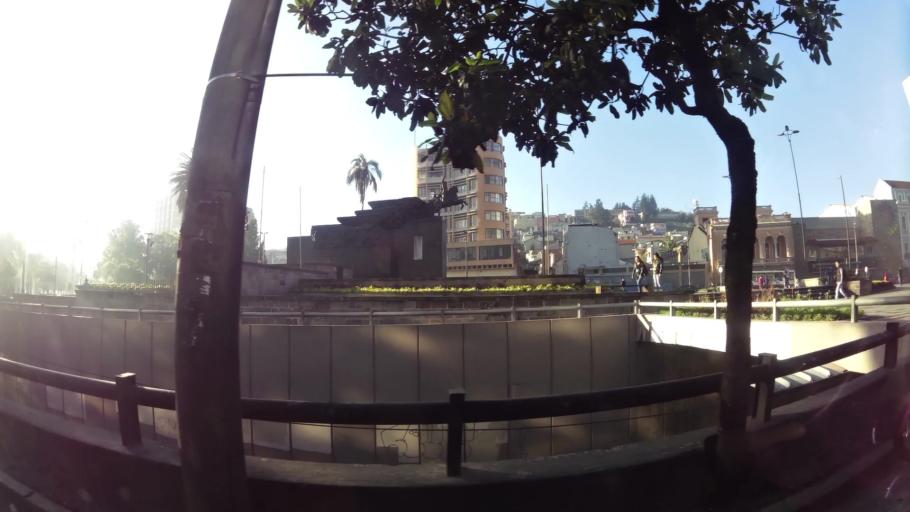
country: EC
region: Pichincha
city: Quito
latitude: -0.2158
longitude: -78.5043
